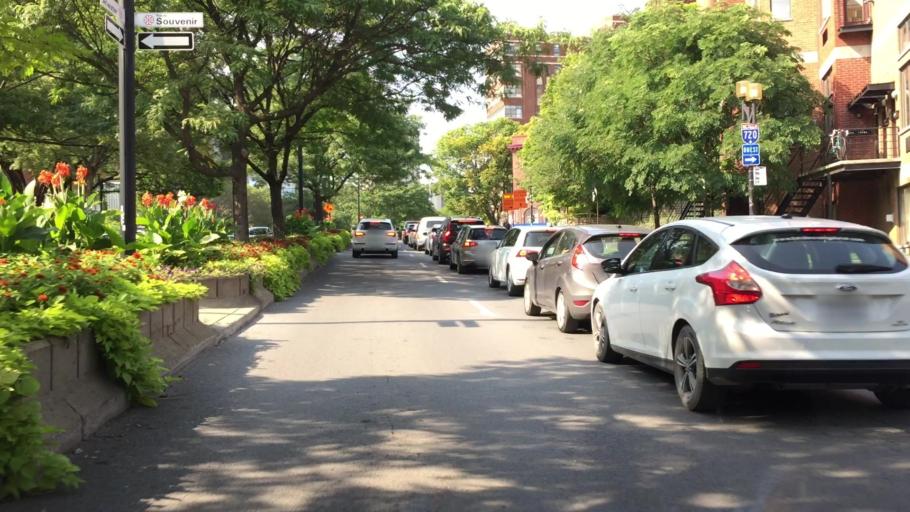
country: CA
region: Quebec
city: Westmount
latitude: 45.4875
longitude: -73.5822
